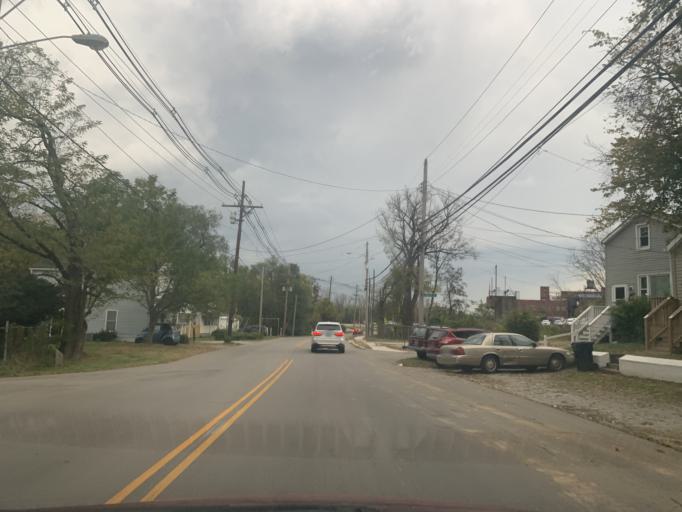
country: US
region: Indiana
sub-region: Clark County
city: Jeffersonville
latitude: 38.2611
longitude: -85.7161
